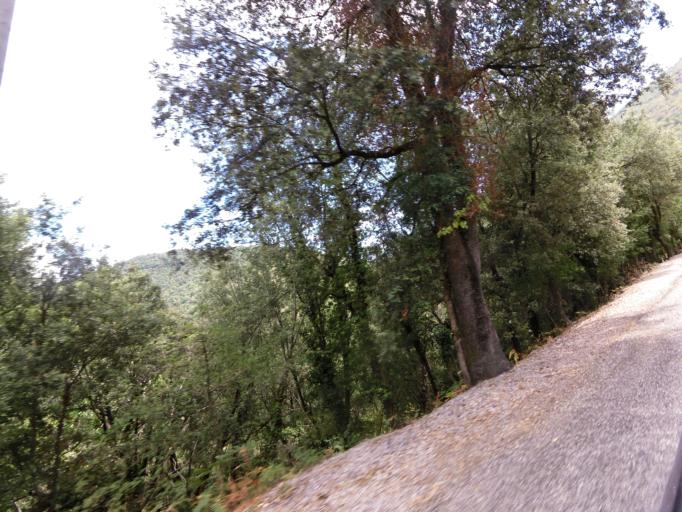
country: FR
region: Languedoc-Roussillon
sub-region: Departement du Gard
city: Le Vigan
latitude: 44.0030
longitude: 3.6577
